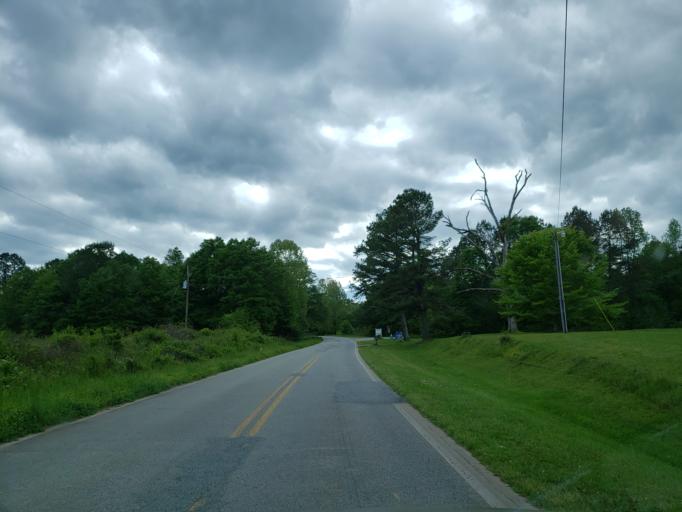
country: US
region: Georgia
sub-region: Haralson County
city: Tallapoosa
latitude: 33.7662
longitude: -85.3244
